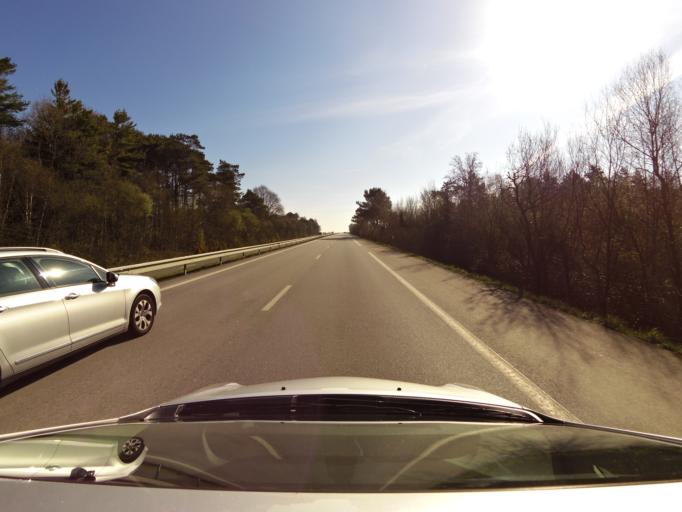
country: FR
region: Brittany
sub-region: Departement du Morbihan
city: Pleugriffet
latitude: 47.9217
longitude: -2.7036
